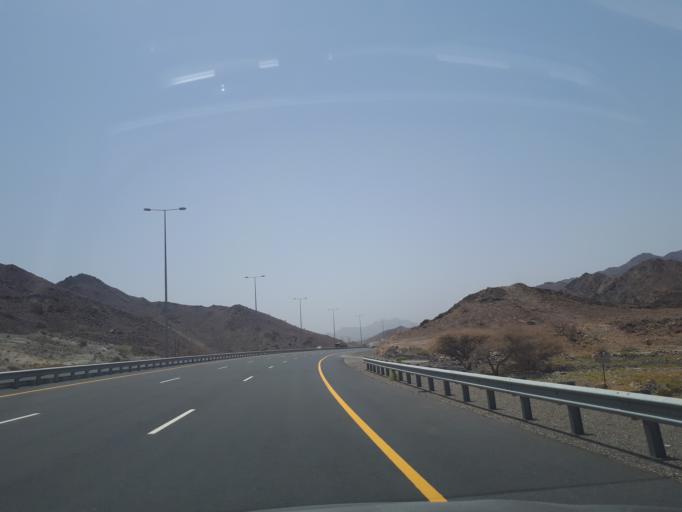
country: OM
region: Ash Sharqiyah
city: Ibra'
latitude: 22.8828
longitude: 58.2948
